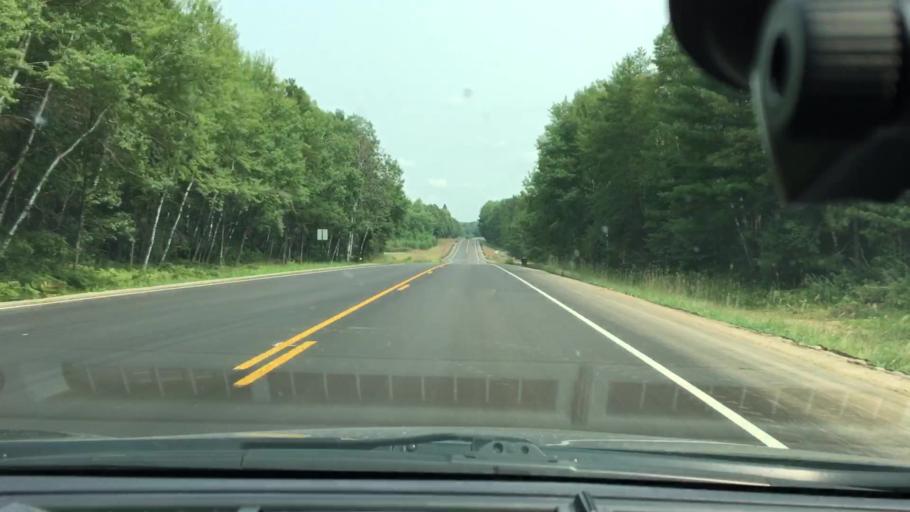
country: US
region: Minnesota
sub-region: Crow Wing County
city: Nisswa
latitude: 46.5294
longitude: -94.2449
